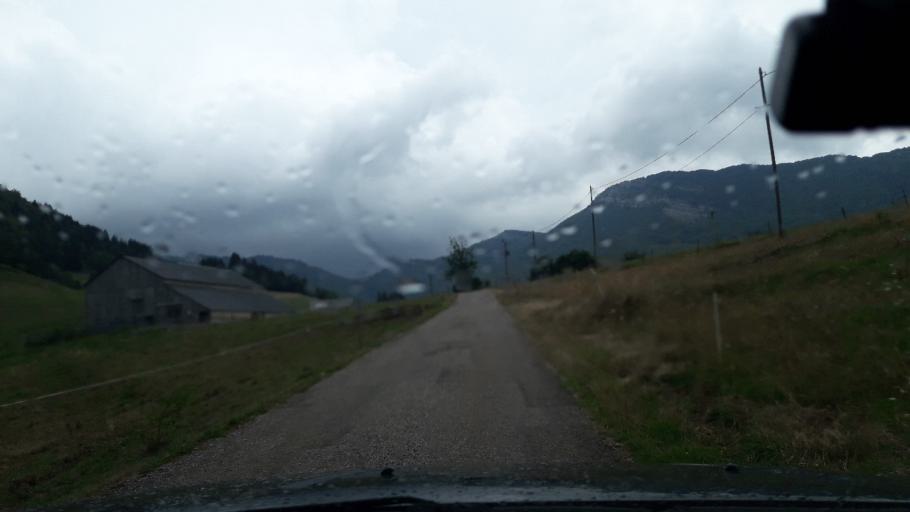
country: FR
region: Rhone-Alpes
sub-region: Departement de la Savoie
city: Vimines
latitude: 45.4702
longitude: 5.8845
